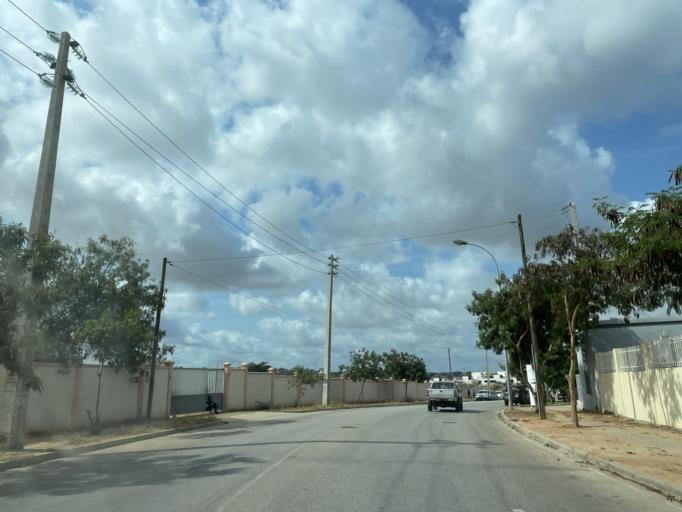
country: AO
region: Luanda
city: Luanda
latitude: -8.9280
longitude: 13.1925
